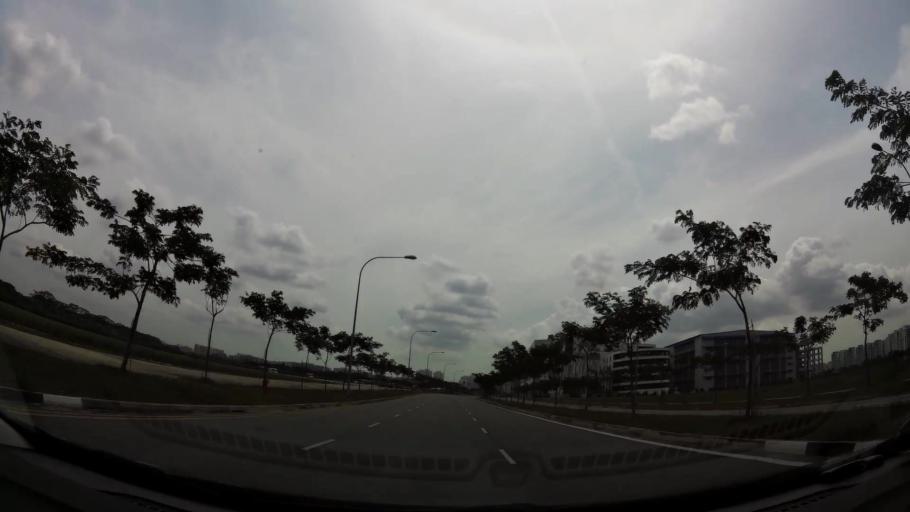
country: MY
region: Johor
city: Johor Bahru
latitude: 1.3591
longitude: 103.7069
